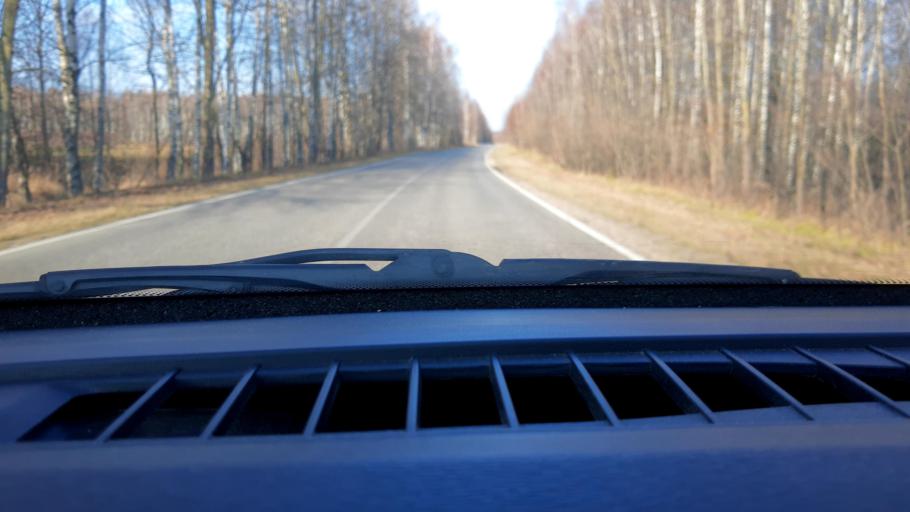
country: RU
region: Nizjnij Novgorod
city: Neklyudovo
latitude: 56.5059
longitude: 43.8438
